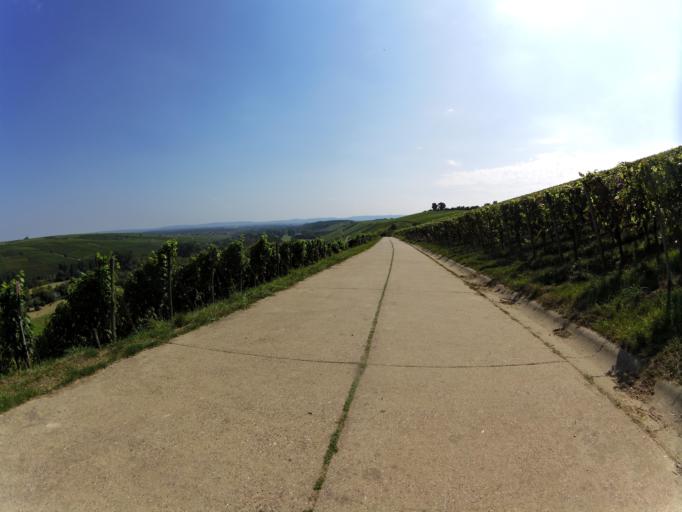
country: DE
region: Bavaria
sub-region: Regierungsbezirk Unterfranken
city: Nordheim
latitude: 49.8415
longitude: 10.1686
